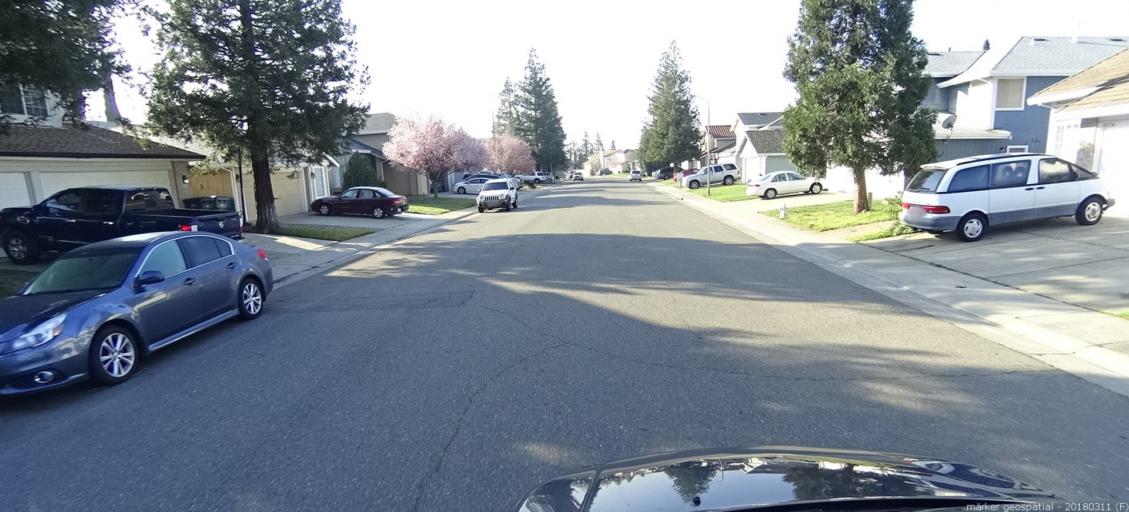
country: US
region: California
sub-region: Sacramento County
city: Vineyard
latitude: 38.4587
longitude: -121.3849
